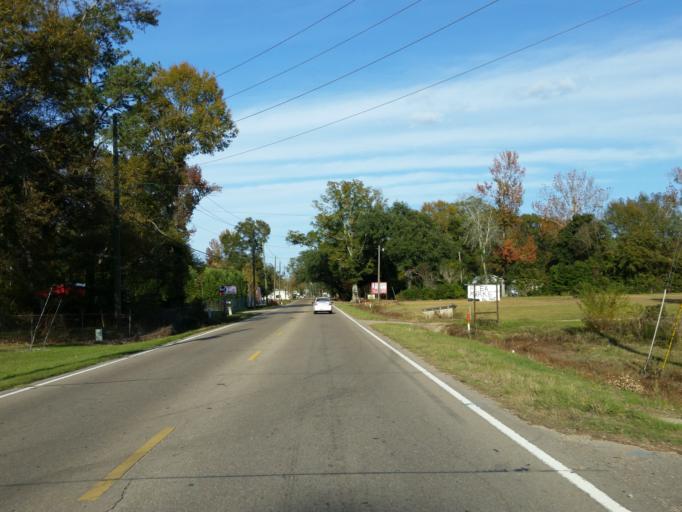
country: US
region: Mississippi
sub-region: Jones County
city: Ellisville
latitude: 31.6502
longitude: -89.1727
